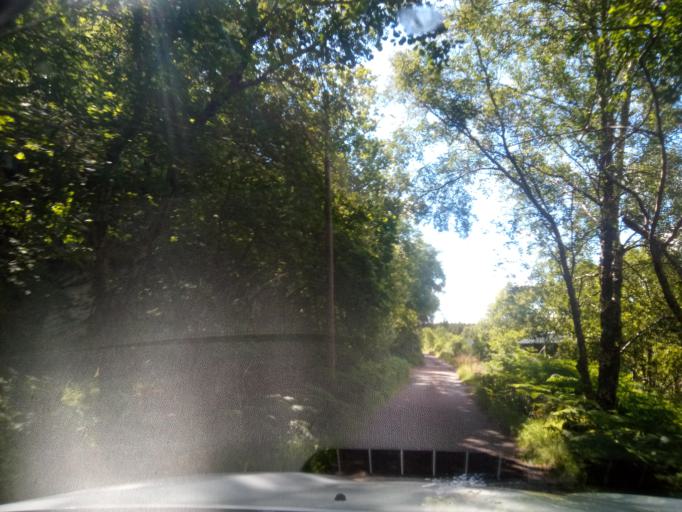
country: GB
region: Scotland
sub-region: Argyll and Bute
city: Isle Of Mull
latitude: 56.7649
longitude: -5.8208
